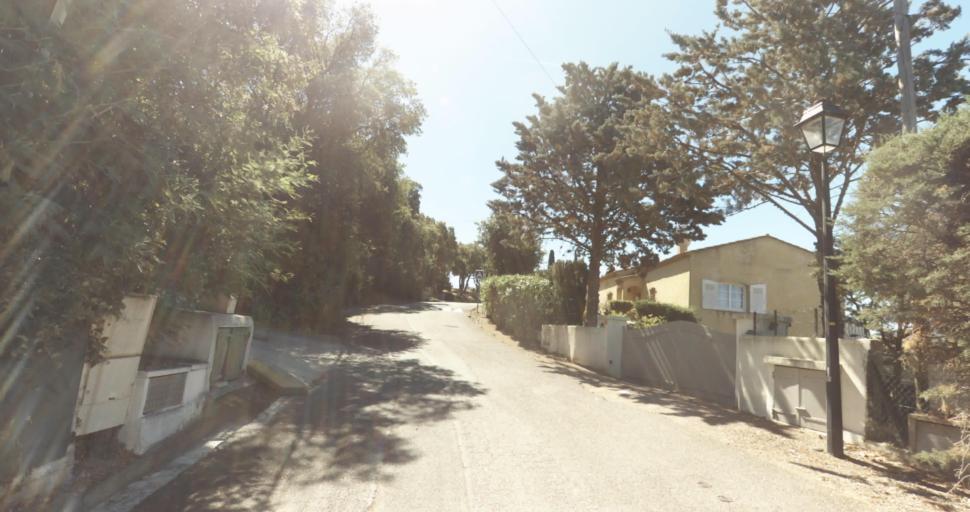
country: FR
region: Provence-Alpes-Cote d'Azur
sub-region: Departement du Var
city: Gassin
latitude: 43.2561
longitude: 6.6013
